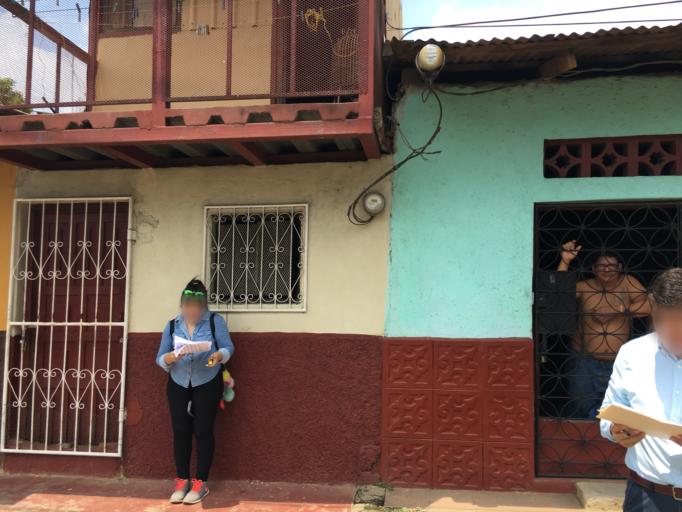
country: NI
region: Masaya
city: Masaya
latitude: 11.9801
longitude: -86.0934
